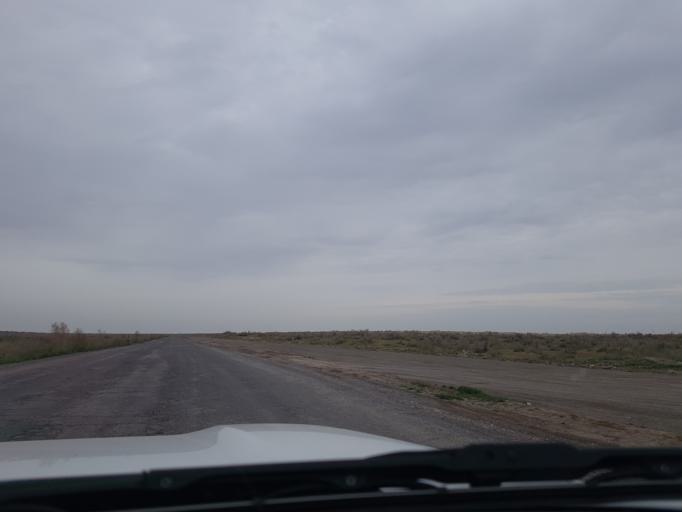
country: TM
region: Lebap
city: Turkmenabat
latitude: 38.7982
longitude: 63.3633
